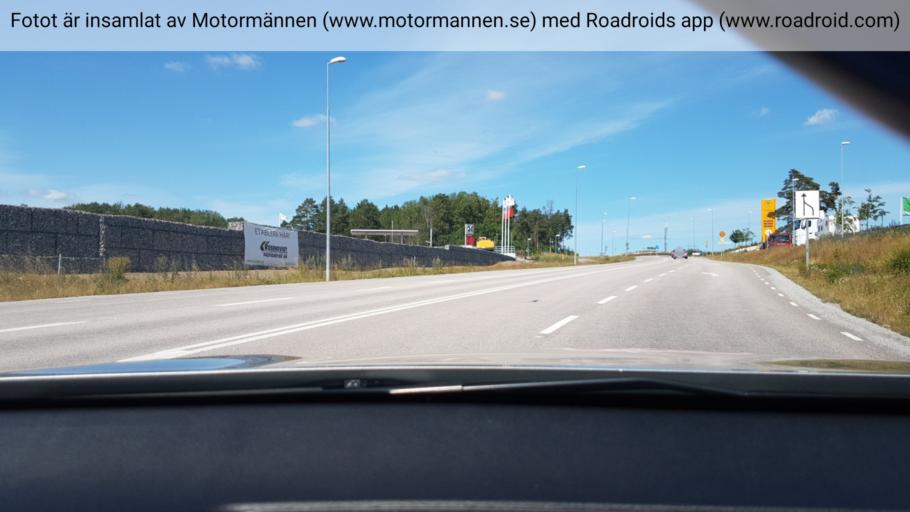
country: SE
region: Stockholm
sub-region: Sigtuna Kommun
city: Rosersberg
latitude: 59.5752
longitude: 17.8958
